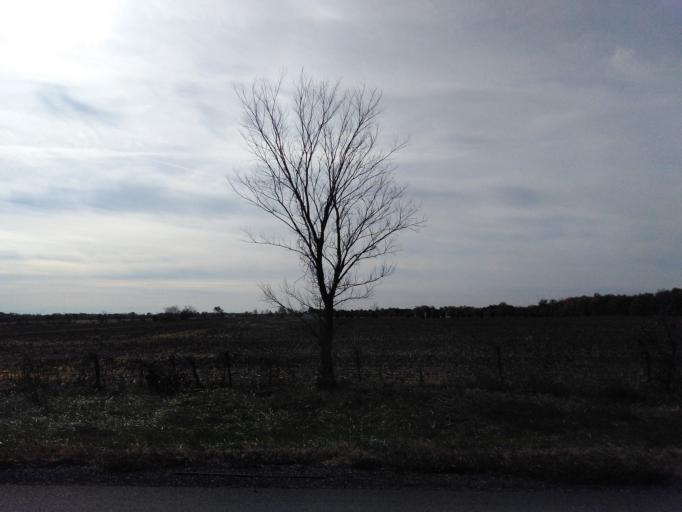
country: US
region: Illinois
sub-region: Madison County
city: Highland
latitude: 38.7863
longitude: -89.6432
